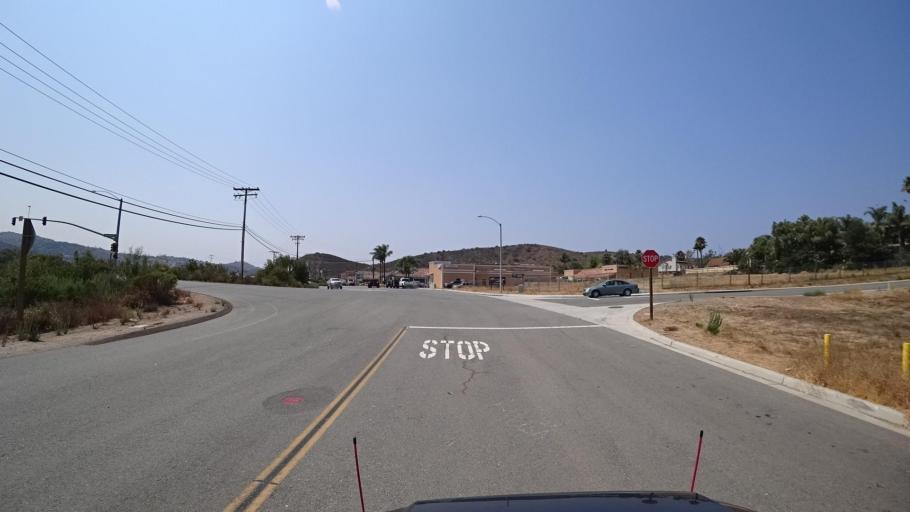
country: US
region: California
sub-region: San Diego County
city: Bonsall
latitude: 33.2917
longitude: -117.2254
